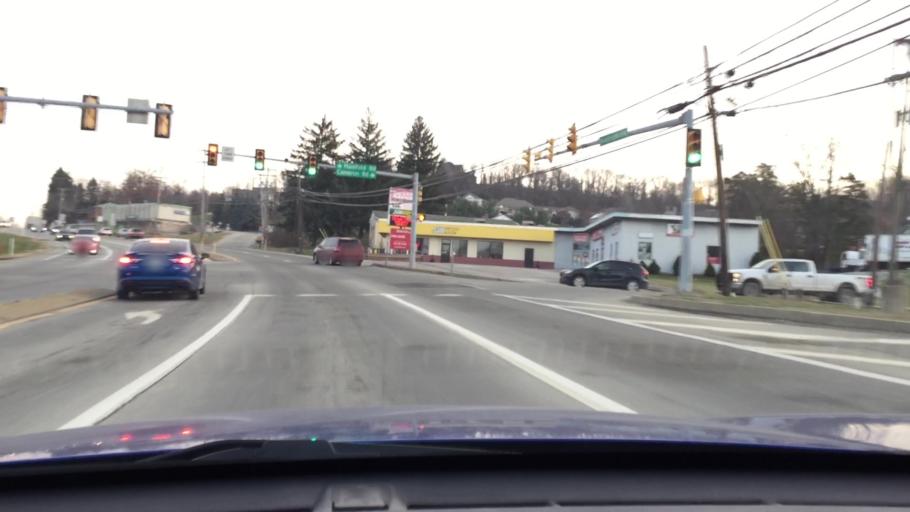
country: US
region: Pennsylvania
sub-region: Washington County
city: East Washington
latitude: 40.1899
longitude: -80.2133
